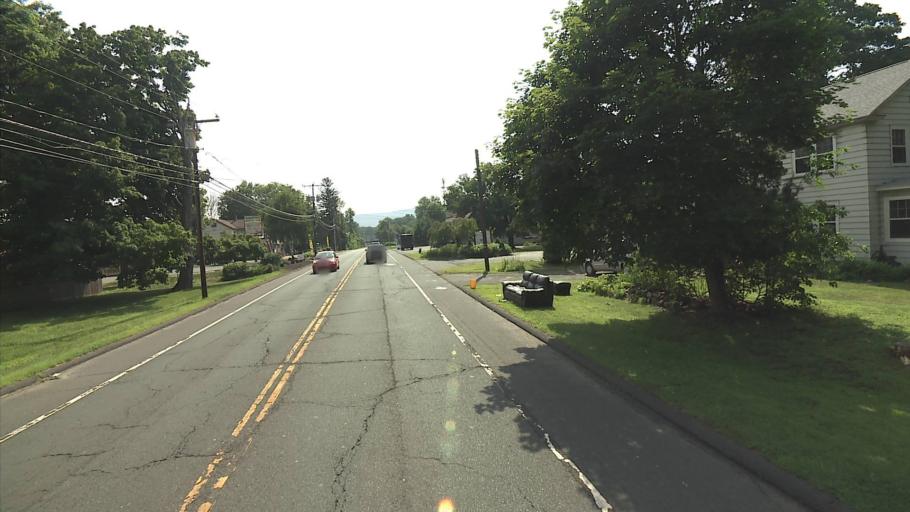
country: US
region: Connecticut
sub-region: New Haven County
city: Cheshire Village
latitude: 41.5645
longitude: -72.8960
